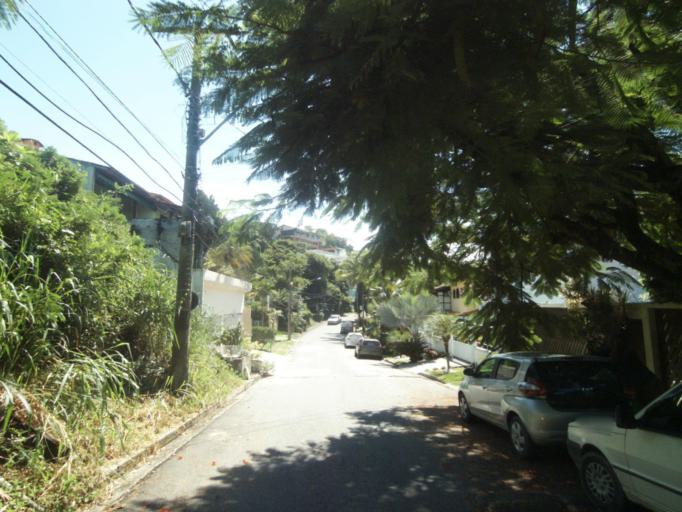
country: BR
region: Rio de Janeiro
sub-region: Niteroi
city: Niteroi
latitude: -22.9570
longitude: -43.0674
